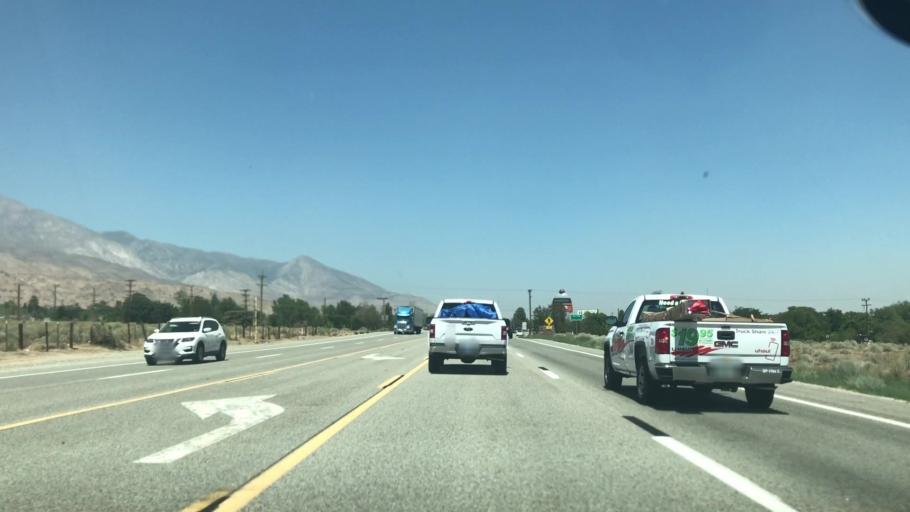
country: US
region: California
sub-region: Inyo County
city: Big Pine
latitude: 37.1538
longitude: -118.2874
